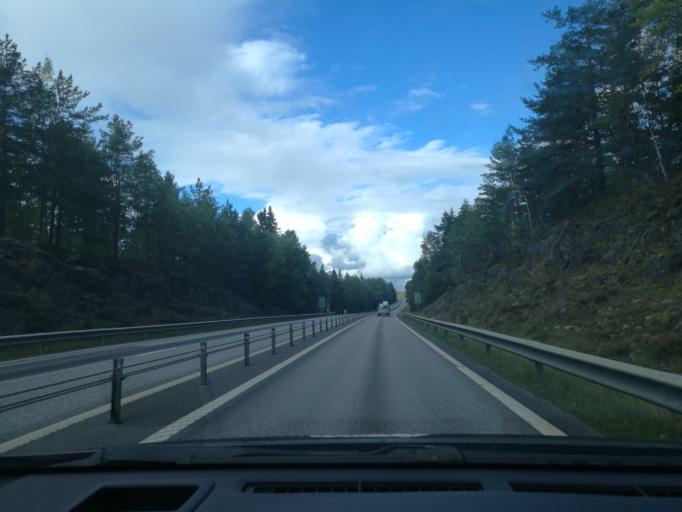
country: SE
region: OEstergoetland
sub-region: Norrkopings Kommun
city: Jursla
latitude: 58.7152
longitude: 16.1640
